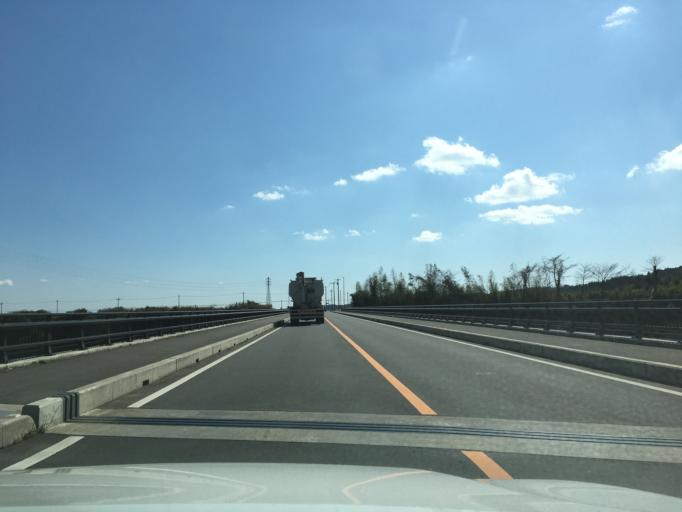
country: JP
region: Tochigi
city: Otawara
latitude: 36.7861
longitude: 140.1168
